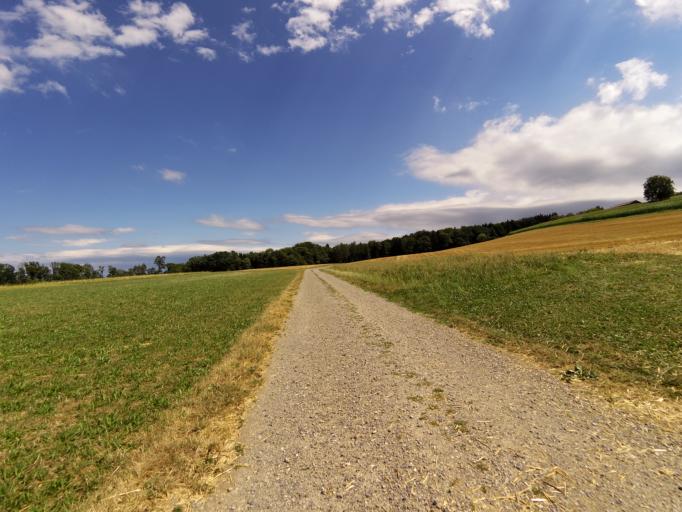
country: CH
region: Thurgau
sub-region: Kreuzlingen District
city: Ermatingen
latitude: 47.6596
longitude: 9.0834
